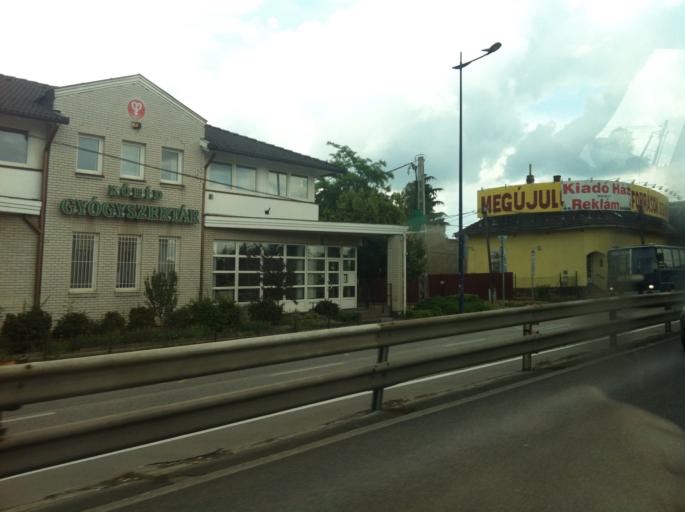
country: HU
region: Budapest
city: Budapest XVIII. keruelet
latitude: 47.4556
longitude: 19.1854
